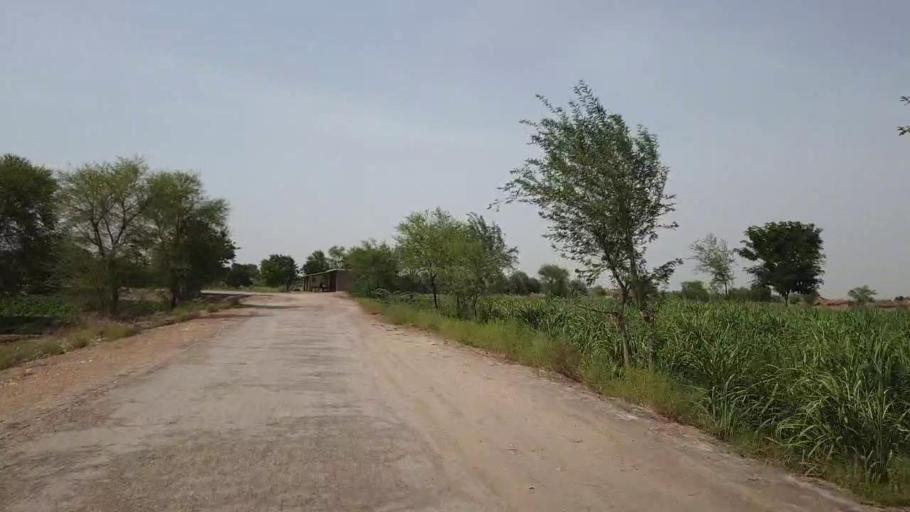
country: PK
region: Sindh
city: Bandhi
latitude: 26.5374
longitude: 68.4077
